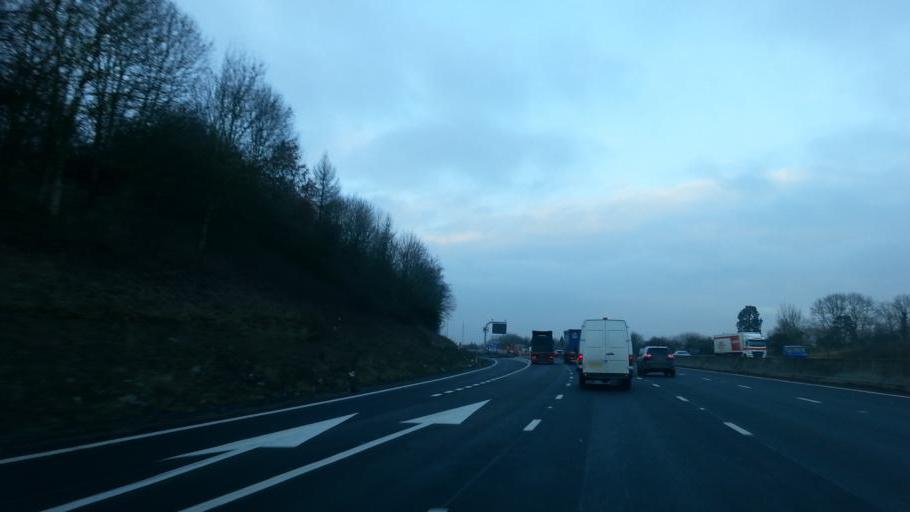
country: GB
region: England
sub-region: Worcestershire
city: Droitwich
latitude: 52.2832
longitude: -2.1193
